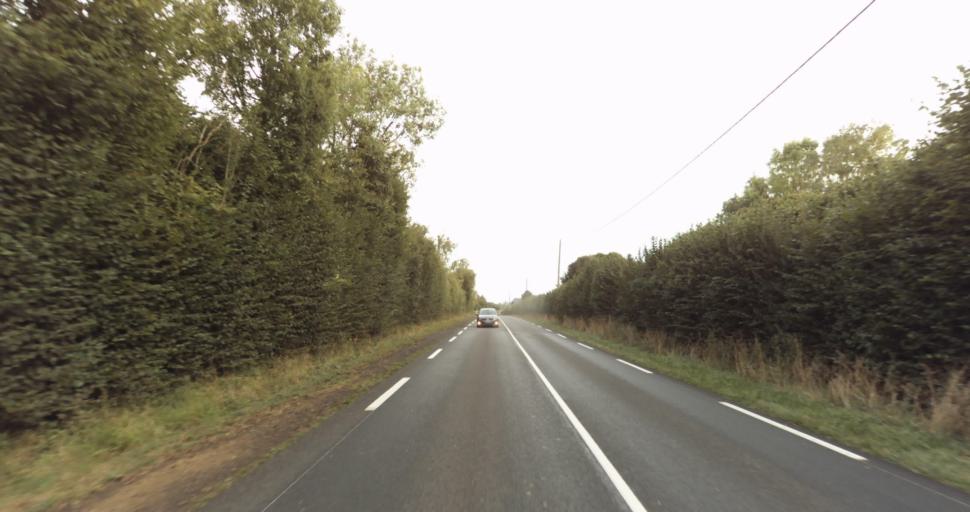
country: FR
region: Lower Normandy
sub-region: Departement de l'Orne
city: Gace
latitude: 48.8604
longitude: 0.2529
